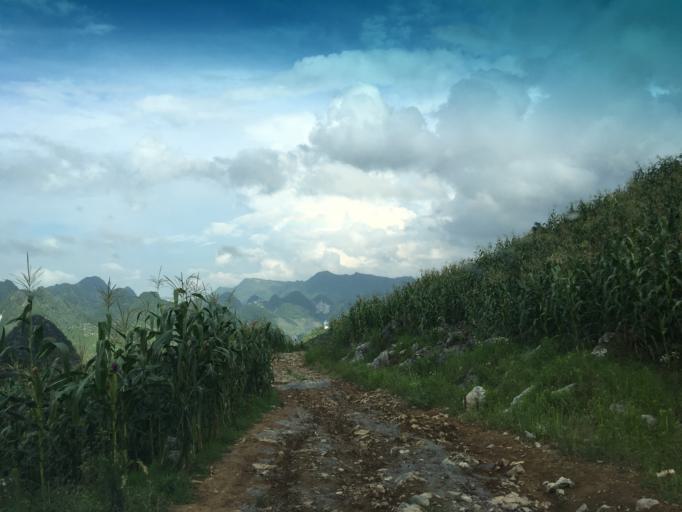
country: CN
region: Guangxi Zhuangzu Zizhiqu
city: Xinzhou
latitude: 24.9919
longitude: 105.6357
